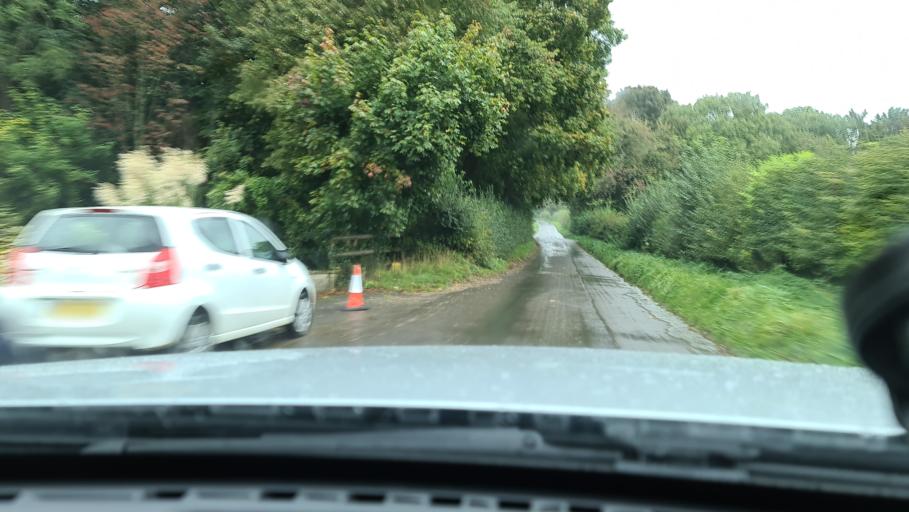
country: GB
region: England
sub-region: Oxfordshire
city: Woodstock
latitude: 51.8920
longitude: -1.3810
